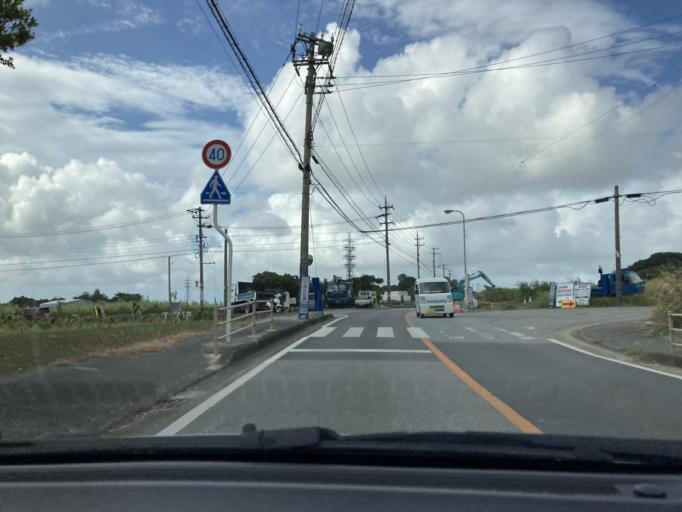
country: JP
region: Okinawa
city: Itoman
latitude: 26.1054
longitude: 127.6952
